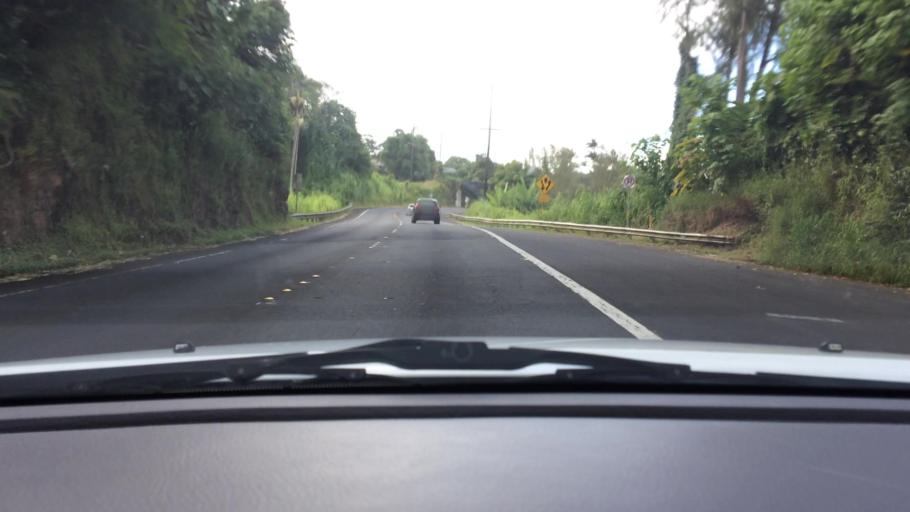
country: US
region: Hawaii
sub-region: Hawaii County
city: Hilo
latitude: 19.7335
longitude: -155.0903
